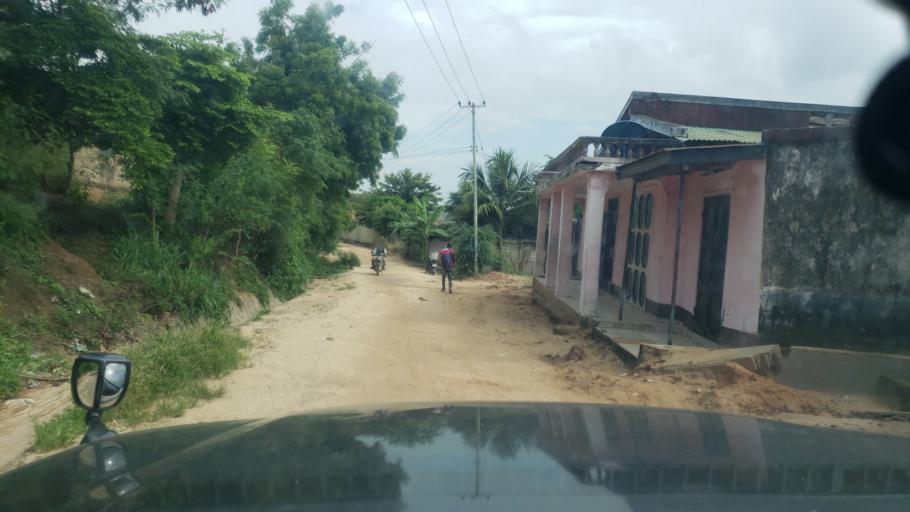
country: TZ
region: Pwani
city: Vikindu
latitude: -6.9208
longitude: 39.2549
